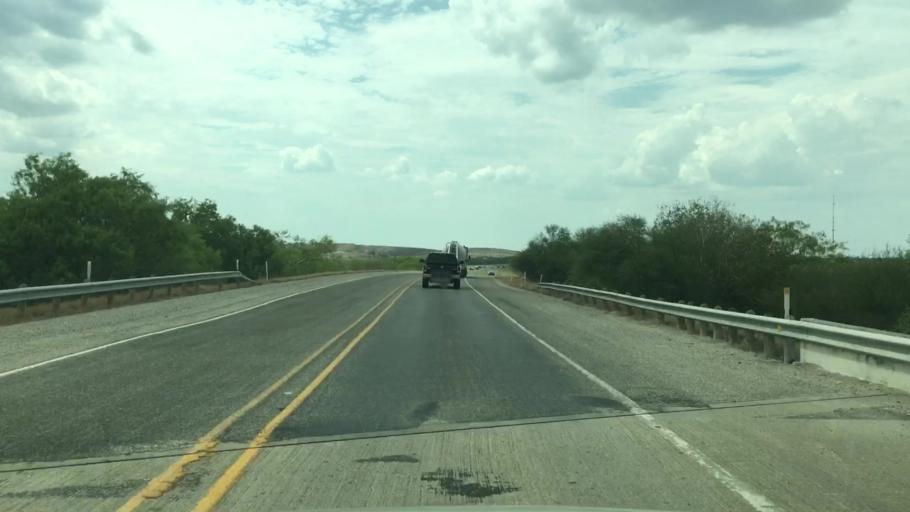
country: US
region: Texas
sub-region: Atascosa County
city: Pleasanton
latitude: 28.7857
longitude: -98.3205
